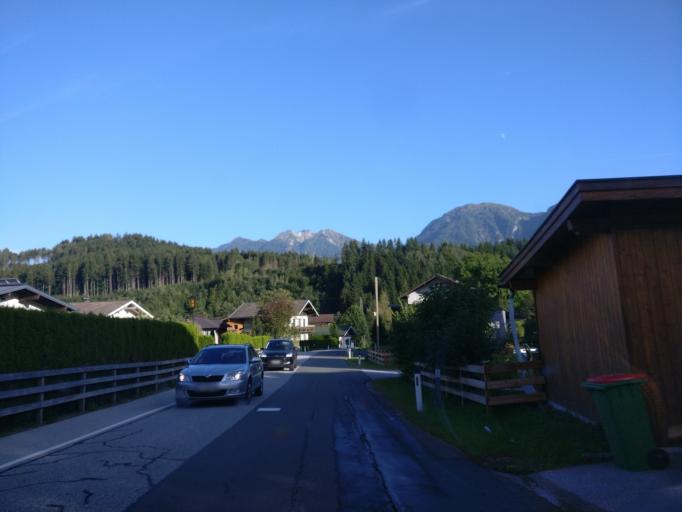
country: AT
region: Salzburg
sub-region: Politischer Bezirk Sankt Johann im Pongau
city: Goldegg
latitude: 47.3289
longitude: 13.0804
